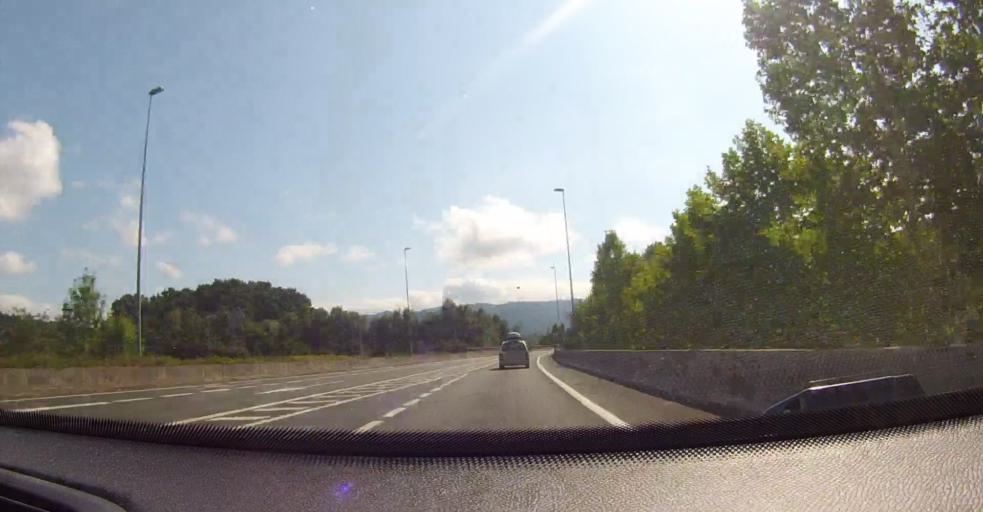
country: ES
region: Basque Country
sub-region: Bizkaia
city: Gernika-Lumo
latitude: 43.3045
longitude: -2.6772
